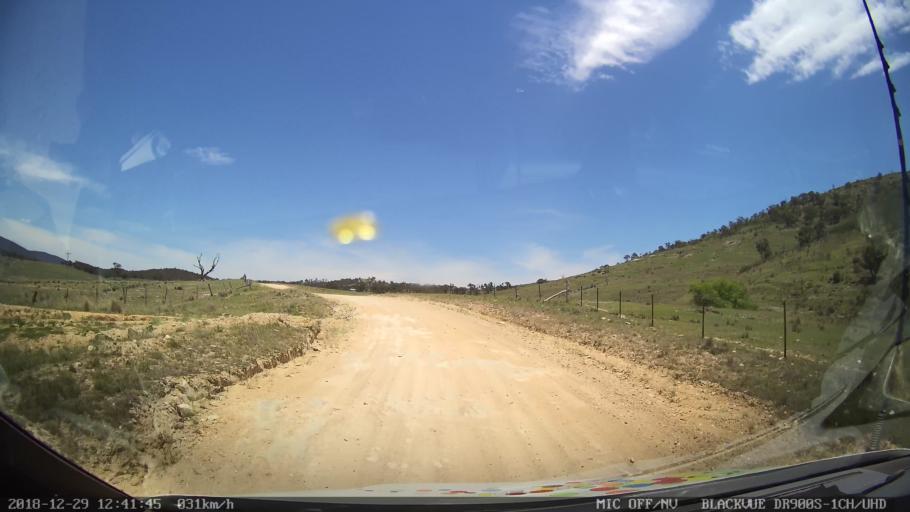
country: AU
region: Australian Capital Territory
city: Macarthur
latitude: -35.6092
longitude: 149.2214
